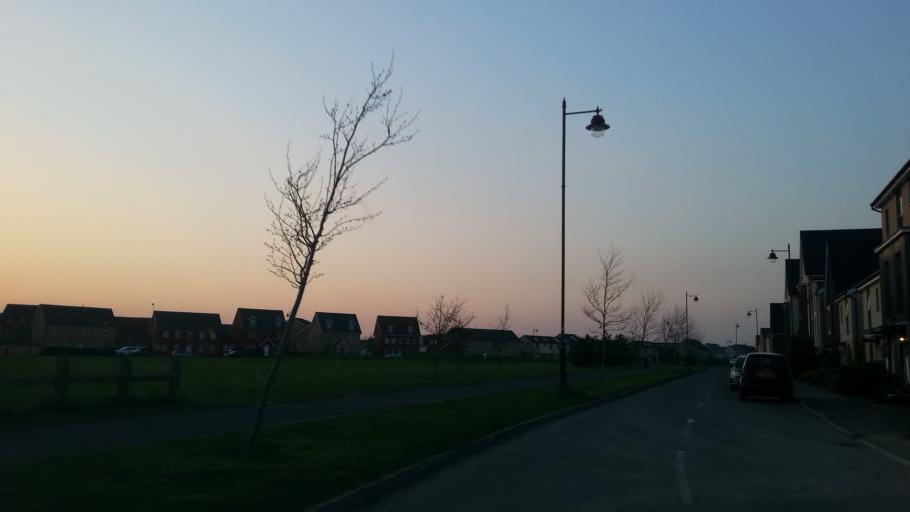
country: GB
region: England
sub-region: Cambridgeshire
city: Papworth Everard
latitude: 52.2163
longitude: -0.0526
